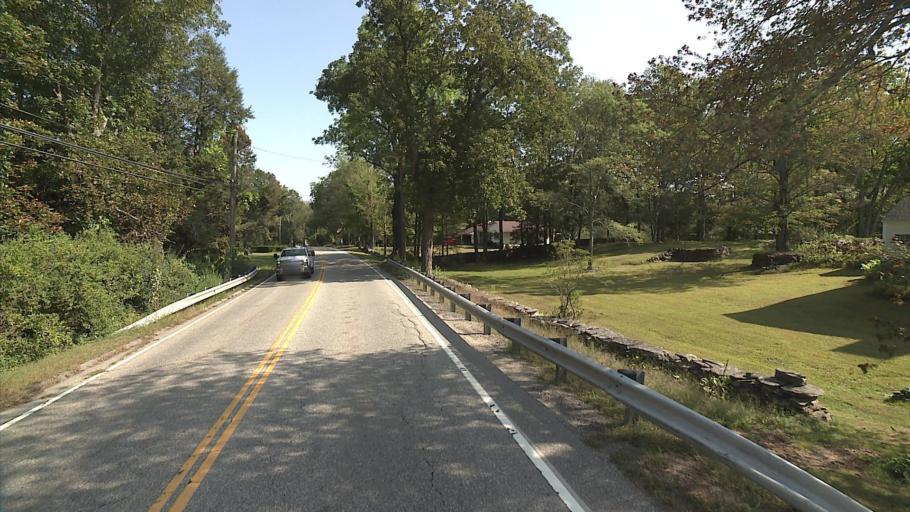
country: US
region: Connecticut
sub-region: New London County
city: Jewett City
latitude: 41.6470
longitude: -71.9847
